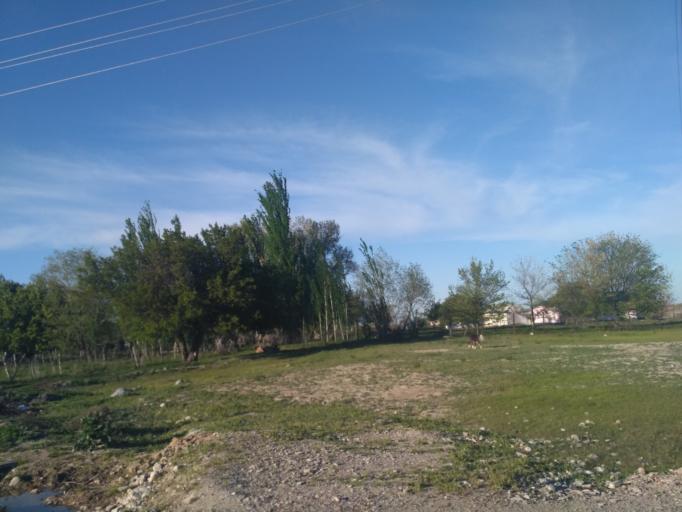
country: KZ
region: Ongtustik Qazaqstan
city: Ashchysay
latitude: 43.6929
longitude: 68.9915
